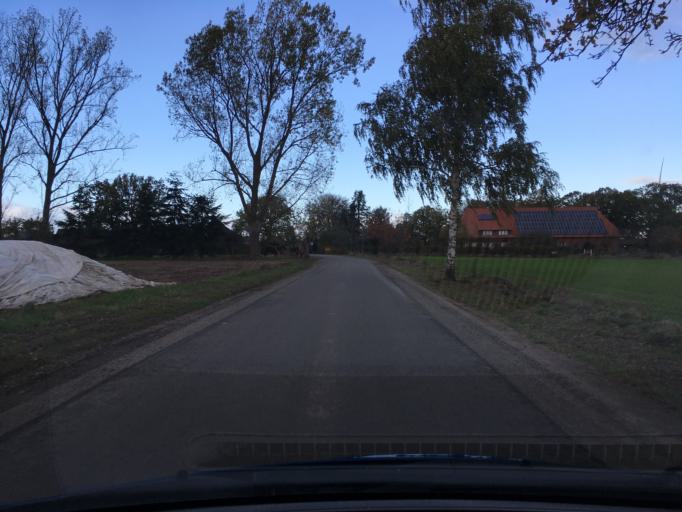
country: DE
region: Lower Saxony
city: Reinstorf
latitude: 53.2482
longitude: 10.5676
